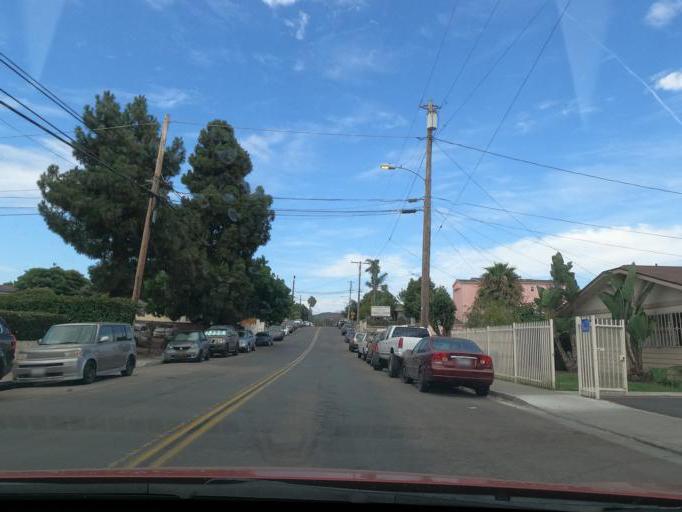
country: US
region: California
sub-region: San Diego County
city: Imperial Beach
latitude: 32.5582
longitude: -117.0536
